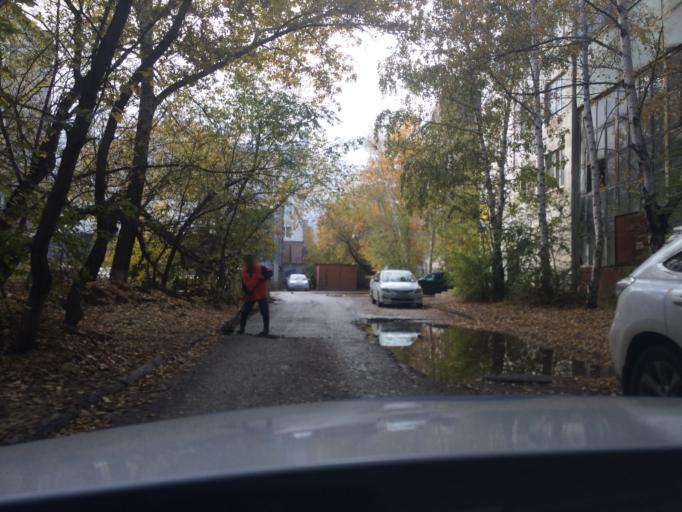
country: KZ
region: Astana Qalasy
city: Astana
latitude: 51.1821
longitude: 71.4245
